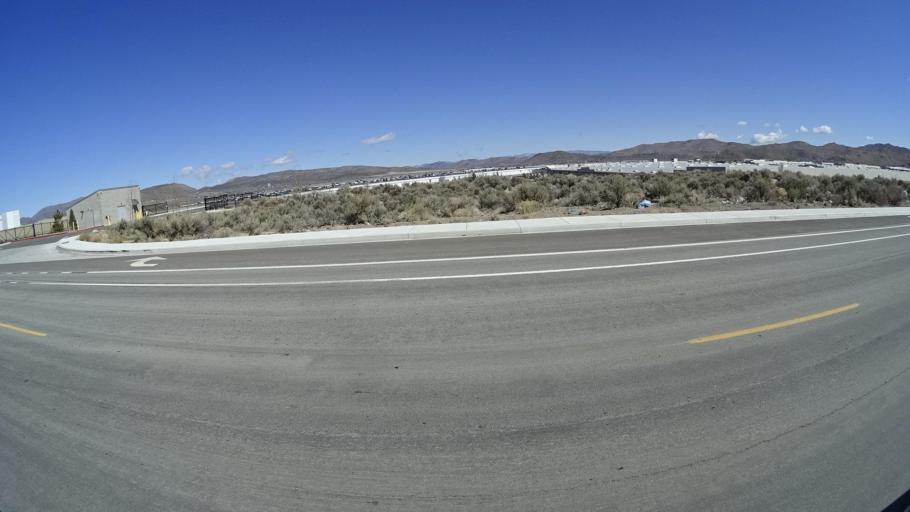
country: US
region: Nevada
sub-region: Washoe County
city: Lemmon Valley
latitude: 39.6467
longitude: -119.8667
